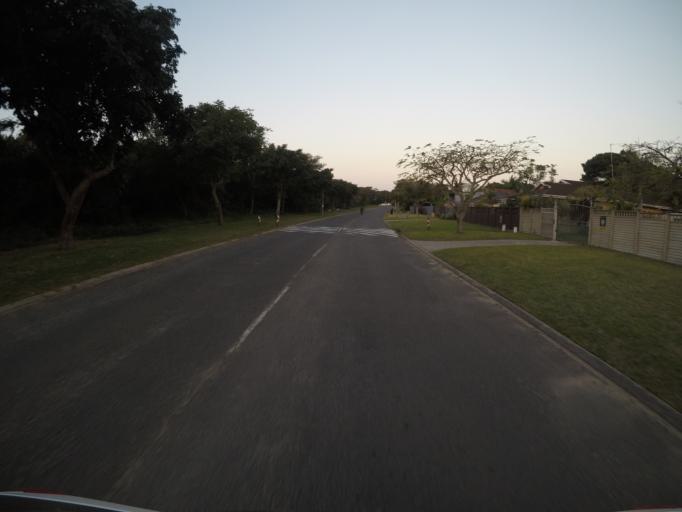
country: ZA
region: KwaZulu-Natal
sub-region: uThungulu District Municipality
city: Richards Bay
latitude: -28.7747
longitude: 32.1204
